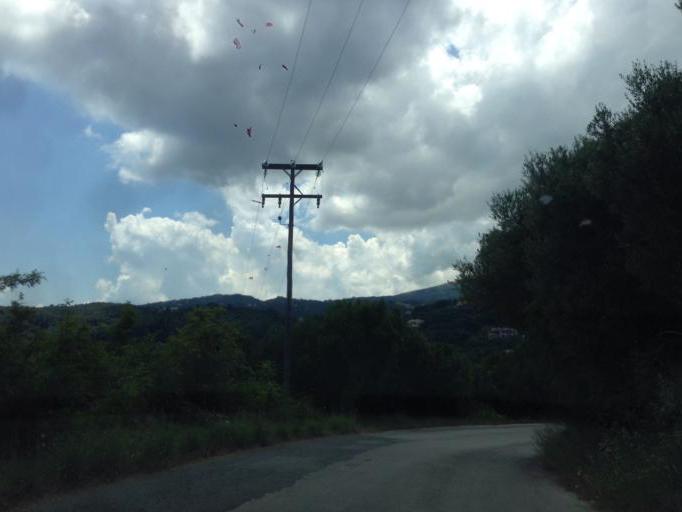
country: AL
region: Vlore
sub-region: Rrethi i Sarandes
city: Xarre
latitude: 39.7702
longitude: 19.9472
